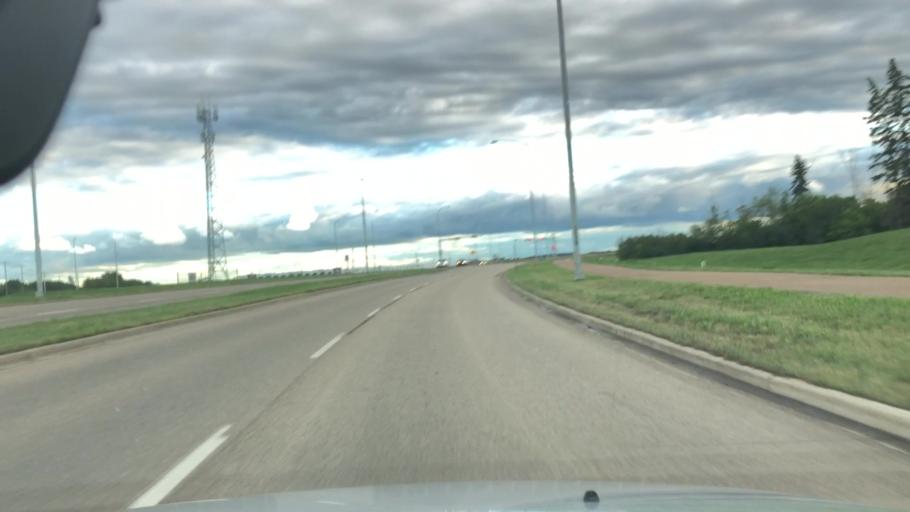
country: CA
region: Alberta
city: St. Albert
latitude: 53.6310
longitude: -113.5663
